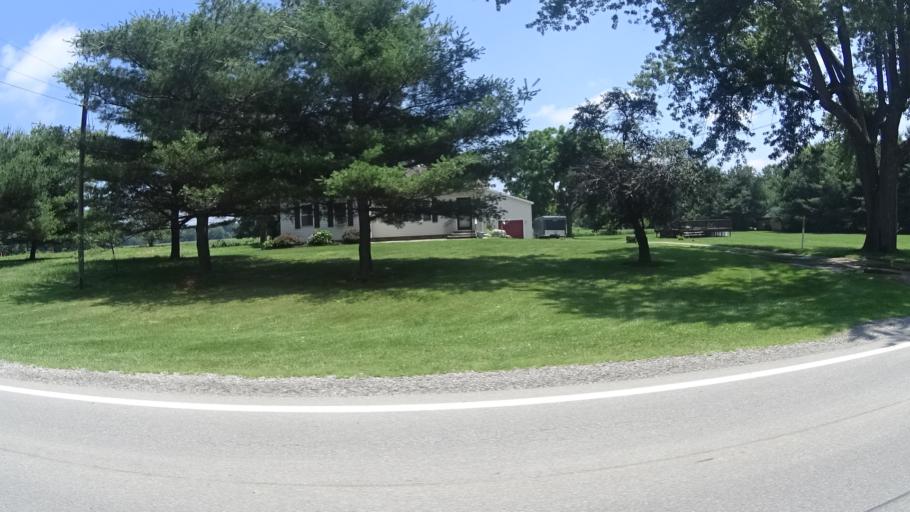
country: US
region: Ohio
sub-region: Lorain County
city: Vermilion
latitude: 41.3572
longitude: -82.3593
